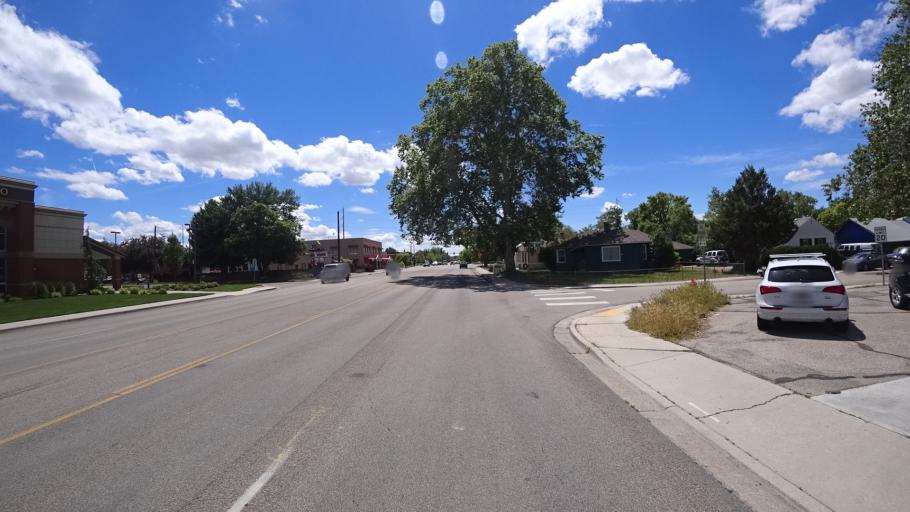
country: US
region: Idaho
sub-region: Ada County
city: Boise
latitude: 43.5915
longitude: -116.2138
